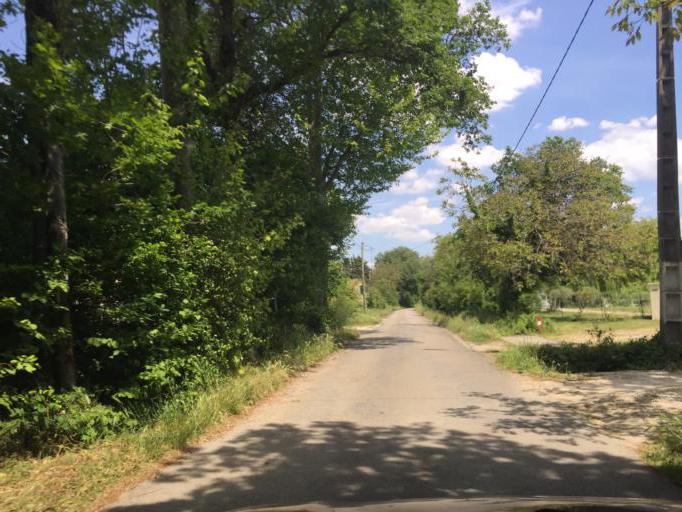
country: FR
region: Provence-Alpes-Cote d'Azur
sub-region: Departement du Vaucluse
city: Jonquieres
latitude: 44.1271
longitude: 4.9073
